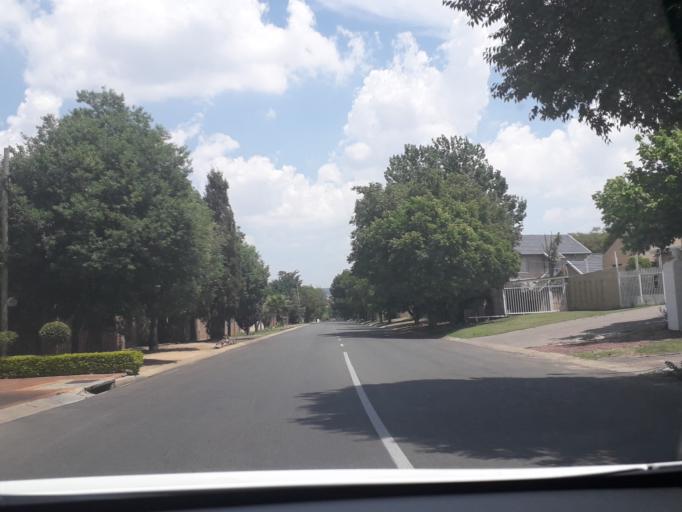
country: ZA
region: Gauteng
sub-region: City of Johannesburg Metropolitan Municipality
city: Midrand
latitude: -26.0398
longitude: 28.0751
